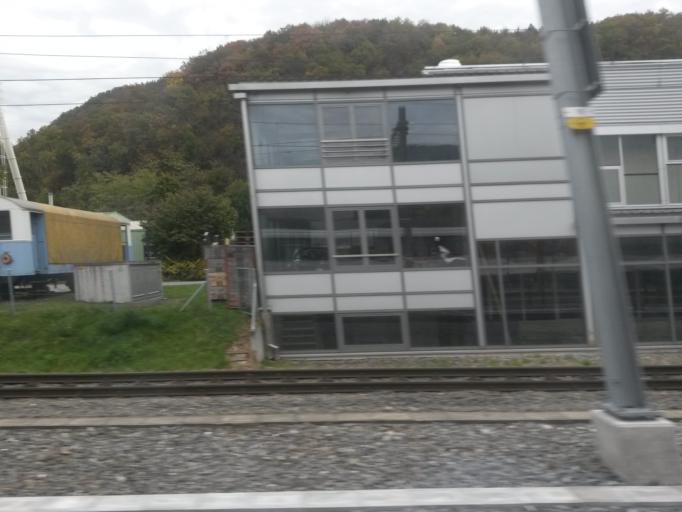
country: CH
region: Vaud
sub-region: Aigle District
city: Aigle
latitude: 46.3065
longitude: 6.9668
